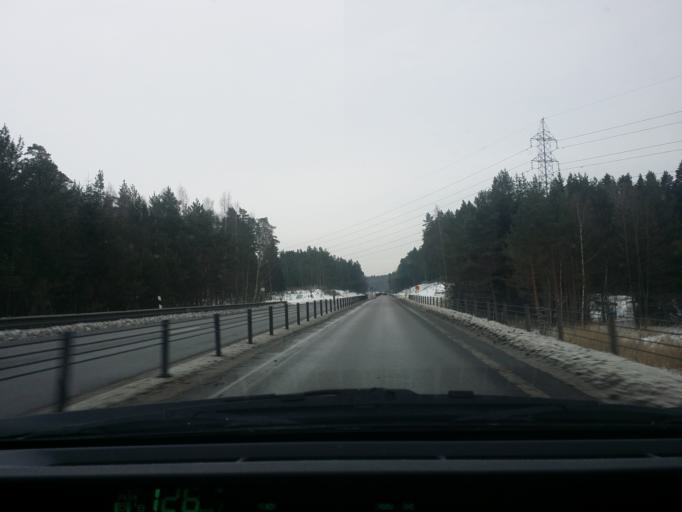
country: SE
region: Vaestra Goetaland
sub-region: Skovde Kommun
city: Stopen
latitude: 58.5094
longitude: 13.8378
